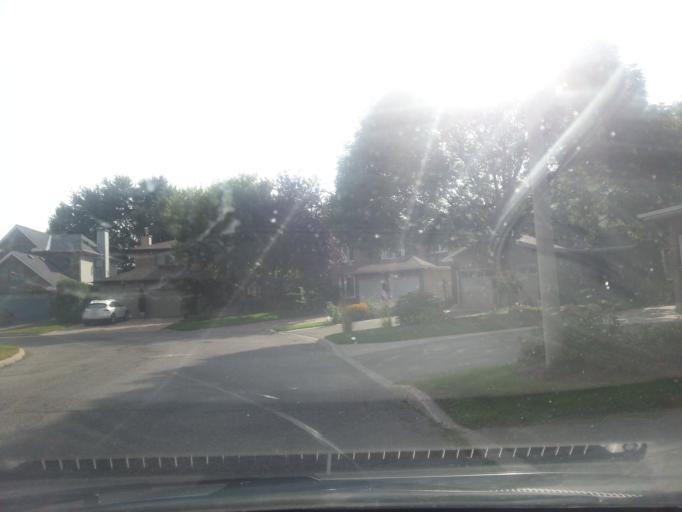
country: CA
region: Quebec
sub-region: Outaouais
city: Gatineau
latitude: 45.4566
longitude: -75.5292
